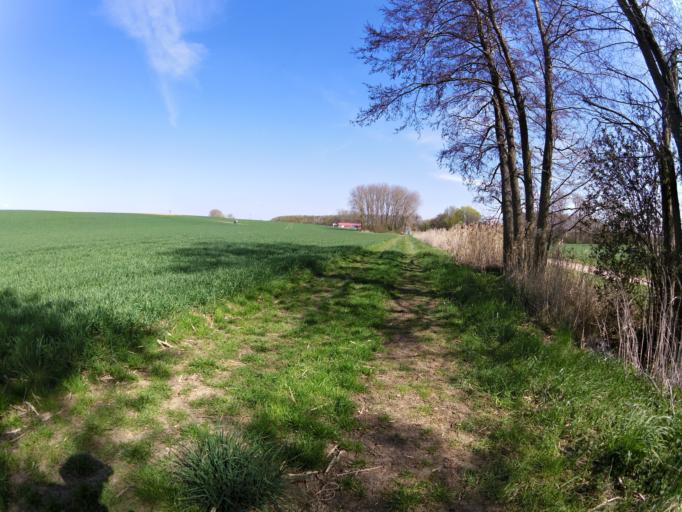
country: DE
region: Bavaria
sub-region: Regierungsbezirk Unterfranken
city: Kurnach
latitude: 49.8644
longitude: 10.0225
